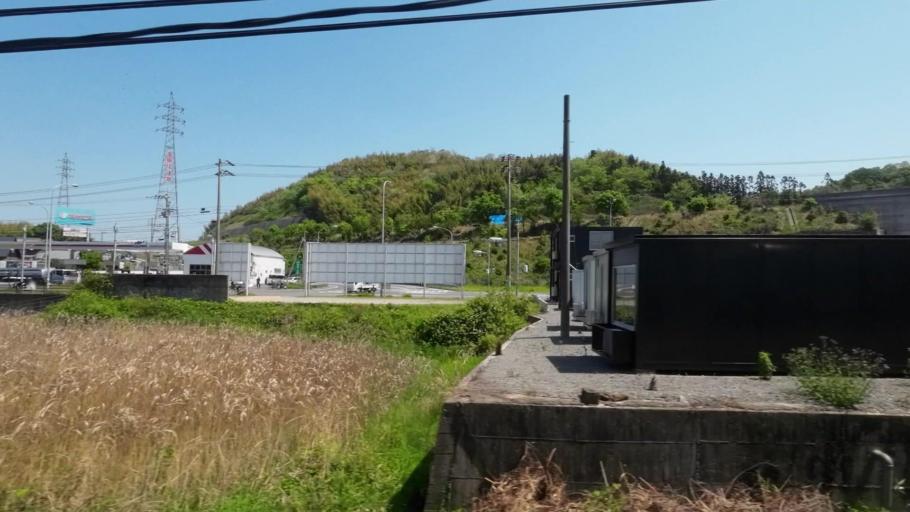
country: JP
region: Ehime
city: Hojo
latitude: 34.0928
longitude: 132.9771
